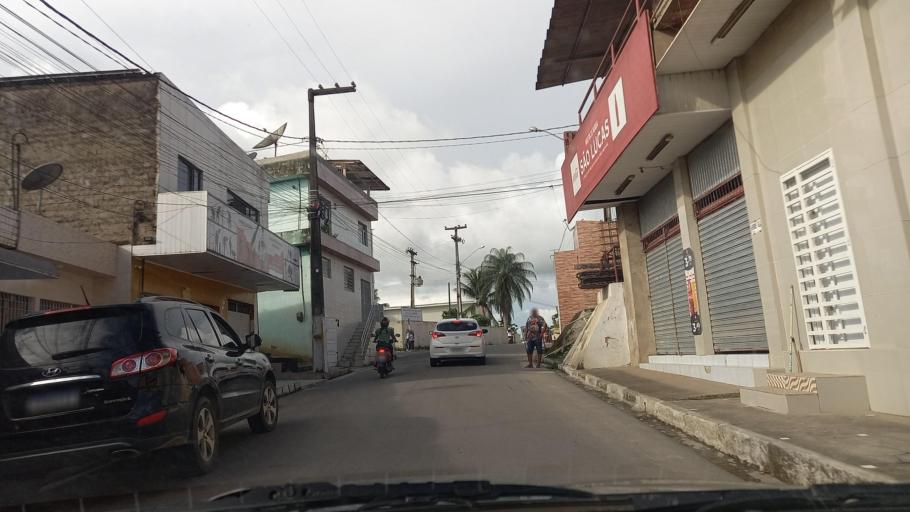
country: BR
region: Pernambuco
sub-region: Palmares
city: Palmares
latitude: -8.6802
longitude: -35.5830
